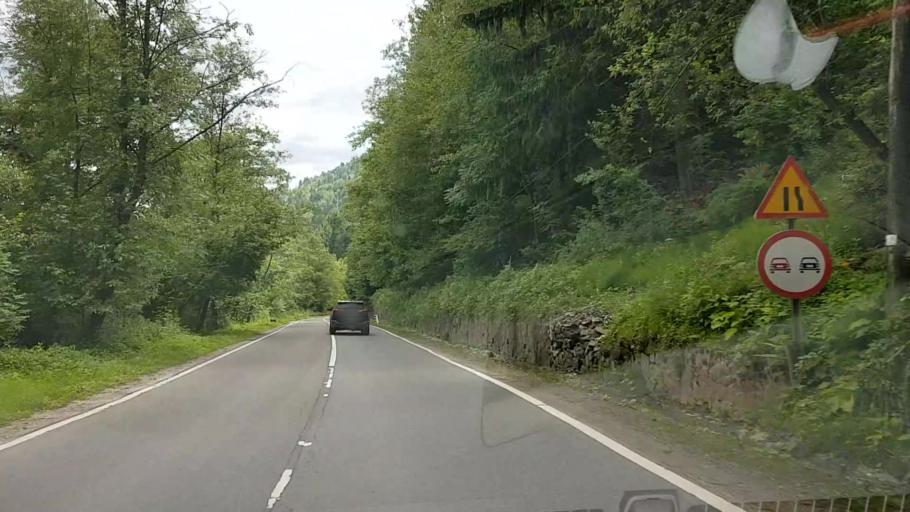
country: RO
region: Neamt
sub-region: Comuna Farcasa
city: Farcasa
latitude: 47.1383
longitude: 25.8612
